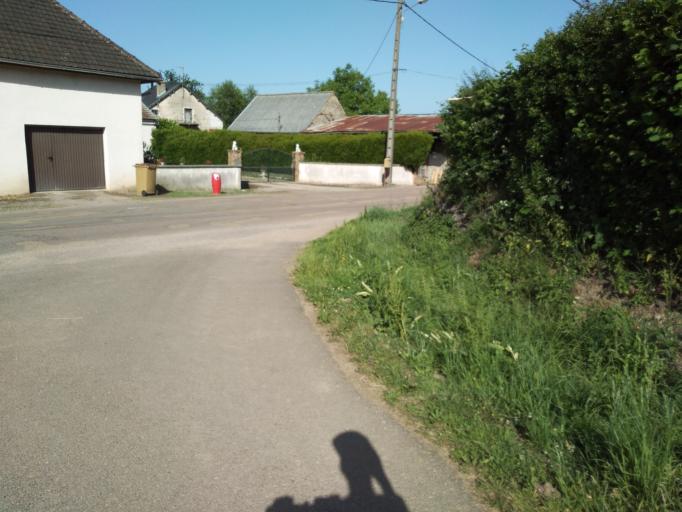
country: FR
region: Bourgogne
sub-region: Departement de la Cote-d'Or
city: Saulieu
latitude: 47.2881
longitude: 4.1376
